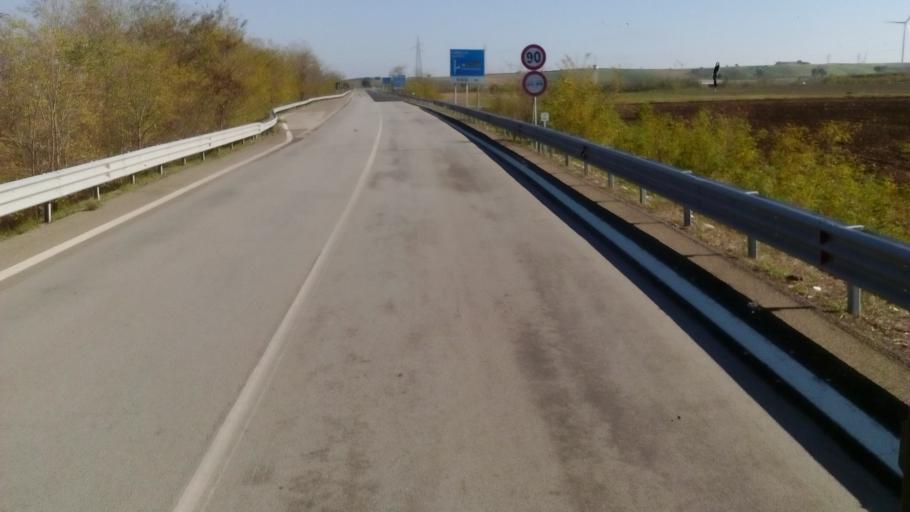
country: IT
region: Basilicate
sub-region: Provincia di Potenza
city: Melfi
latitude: 41.0660
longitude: 15.6691
